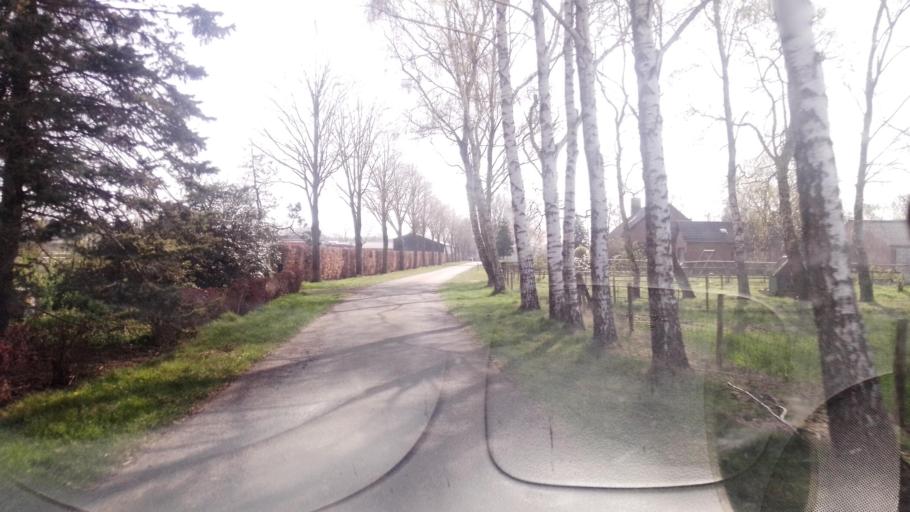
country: NL
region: Limburg
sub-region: Gemeente Peel en Maas
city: Maasbree
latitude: 51.3830
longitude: 5.9864
